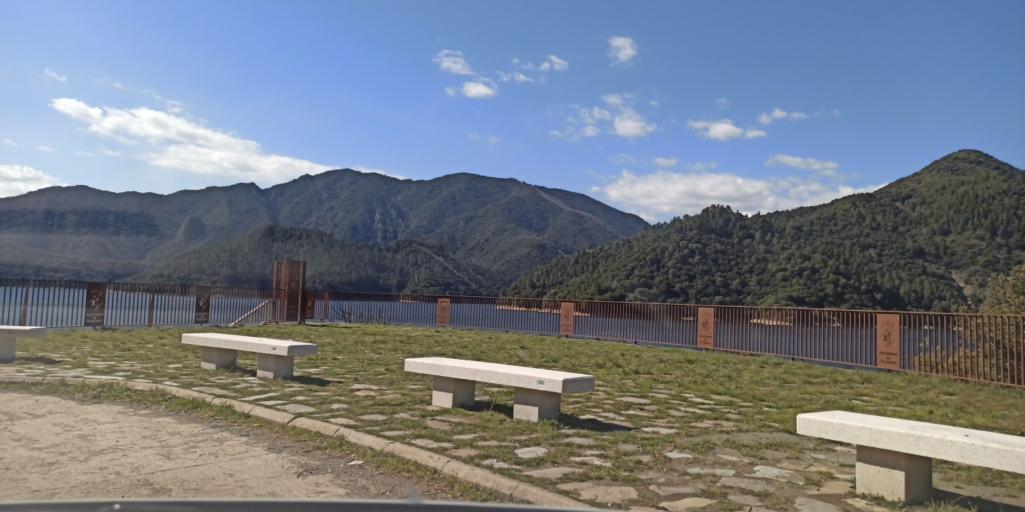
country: ES
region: Catalonia
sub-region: Provincia de Girona
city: Susqueda
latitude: 41.9777
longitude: 2.5237
